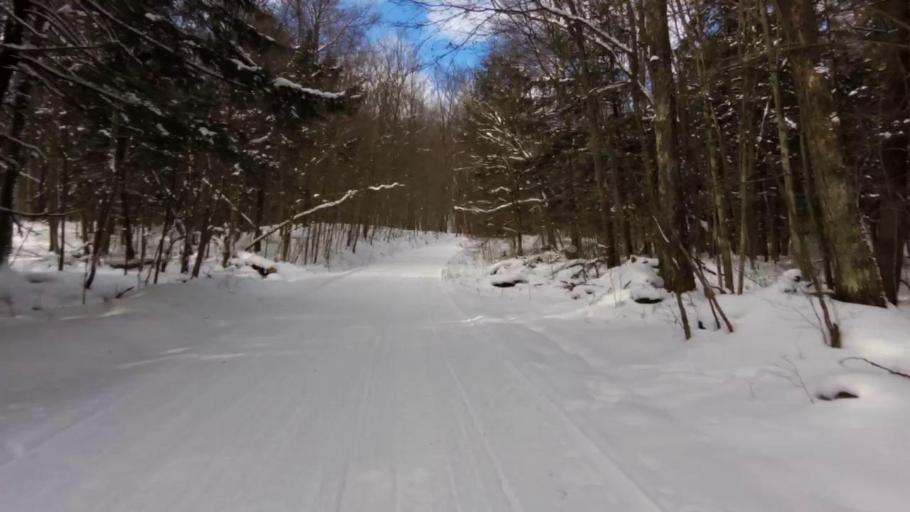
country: US
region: Pennsylvania
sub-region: McKean County
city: Bradford
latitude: 42.0276
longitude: -78.7015
